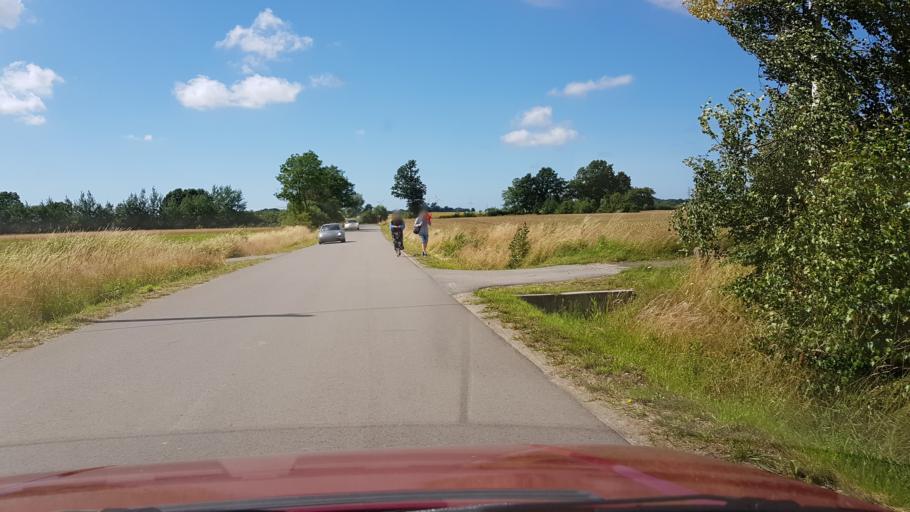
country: PL
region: West Pomeranian Voivodeship
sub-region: Powiat bialogardzki
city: Karlino
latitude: 54.1672
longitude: 15.9212
